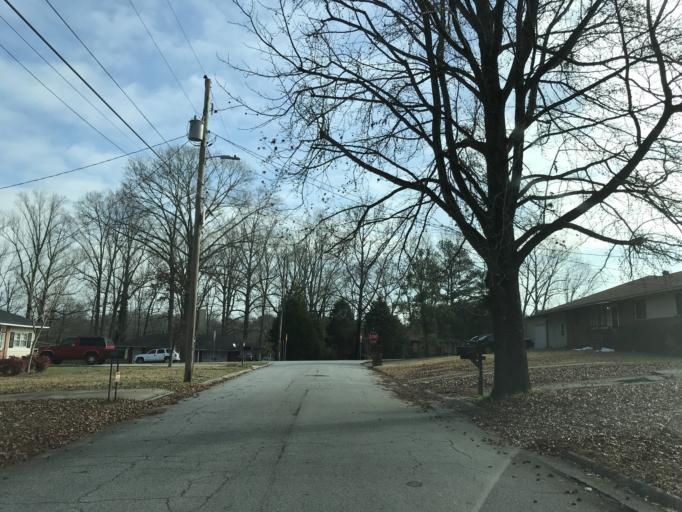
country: US
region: Georgia
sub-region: Clayton County
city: Morrow
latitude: 33.5568
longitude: -84.3636
